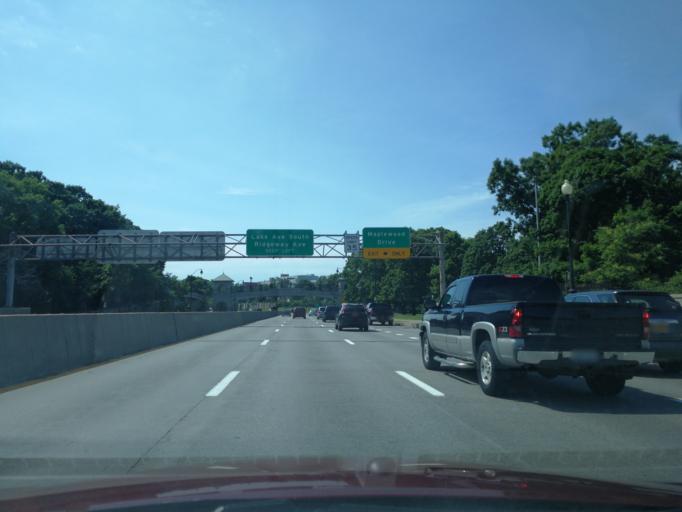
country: US
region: New York
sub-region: Monroe County
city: Rochester
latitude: 43.1932
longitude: -77.6217
